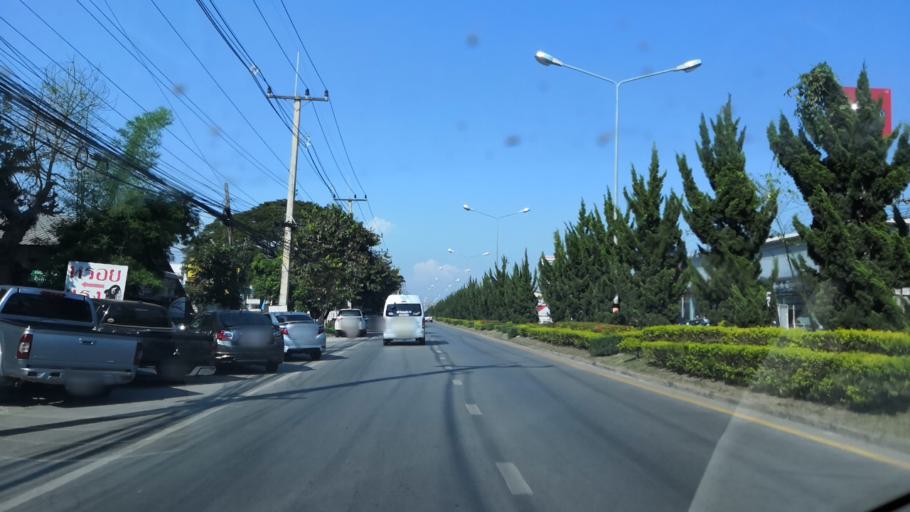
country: TH
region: Chiang Rai
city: Chiang Rai
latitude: 19.9301
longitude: 99.8444
